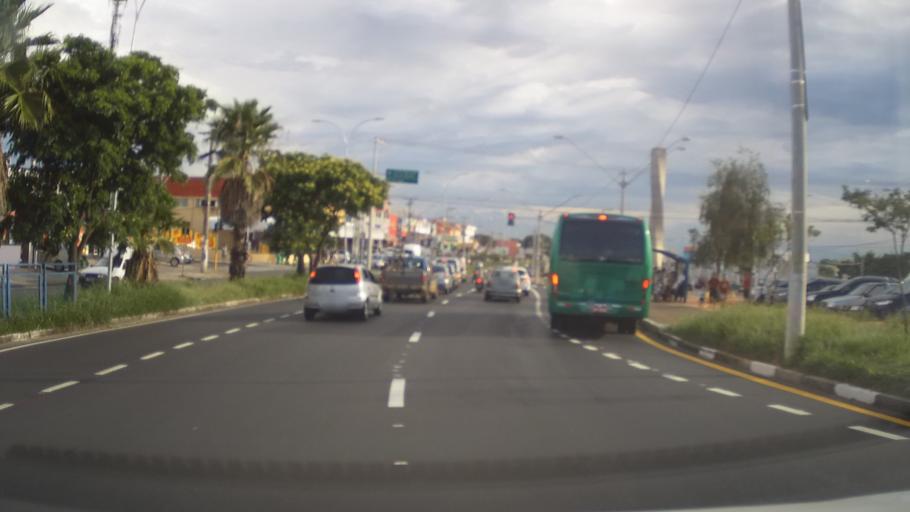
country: BR
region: Sao Paulo
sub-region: Hortolandia
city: Hortolandia
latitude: -22.9473
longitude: -47.1867
